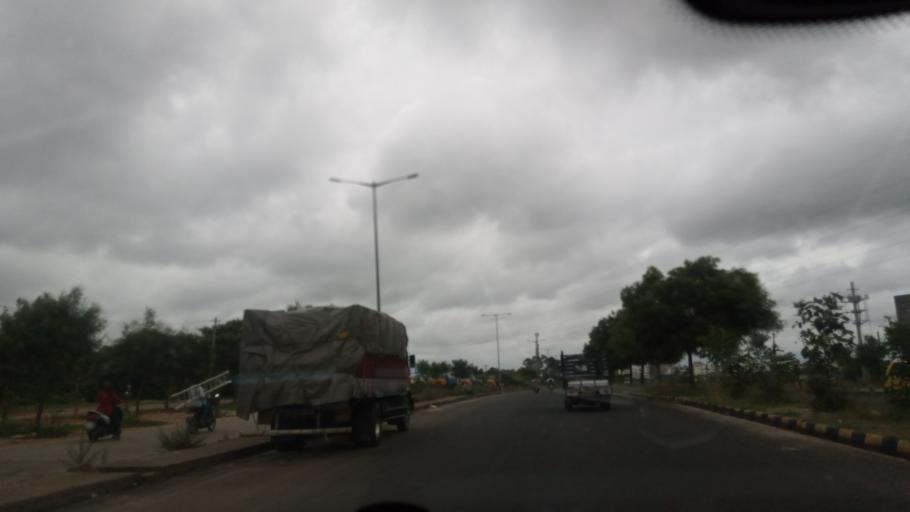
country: IN
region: Karnataka
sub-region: Mysore
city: Mysore
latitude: 12.3146
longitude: 76.5955
